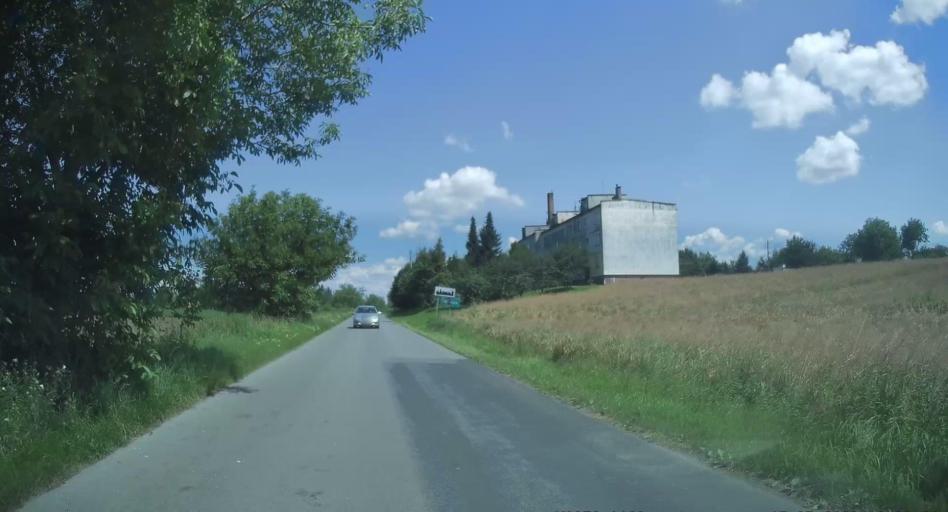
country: PL
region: Subcarpathian Voivodeship
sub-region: Powiat jaroslawski
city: Sosnica
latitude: 49.8596
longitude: 22.8809
